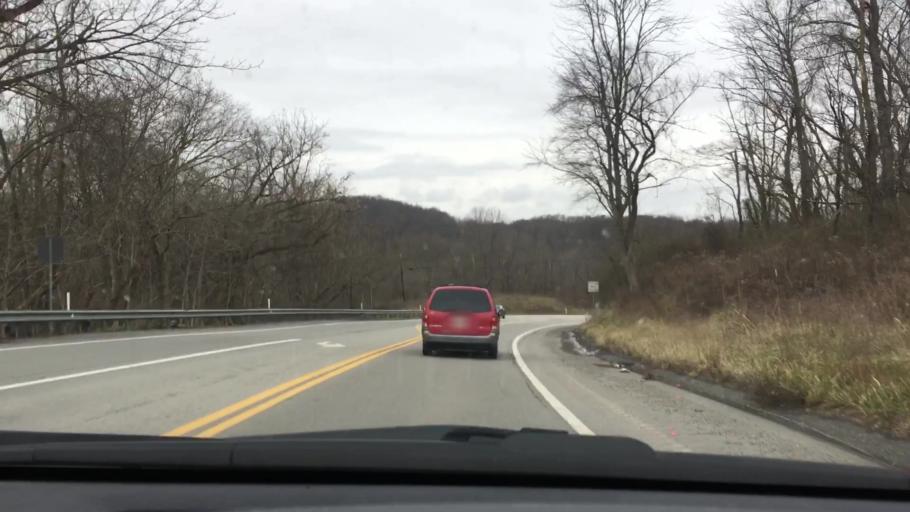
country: US
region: Pennsylvania
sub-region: Fayette County
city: Masontown
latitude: 39.8503
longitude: -79.9206
